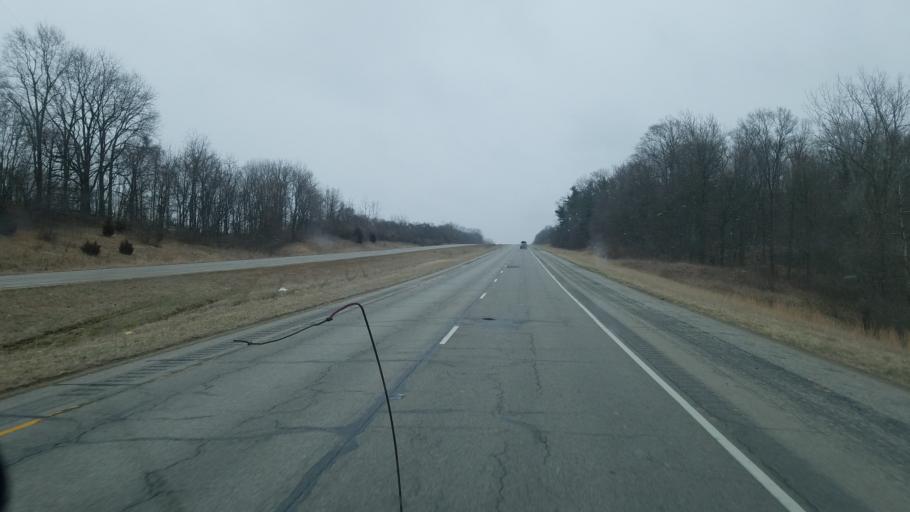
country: US
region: Indiana
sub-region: Wabash County
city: Wabash
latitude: 40.8051
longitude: -85.9179
